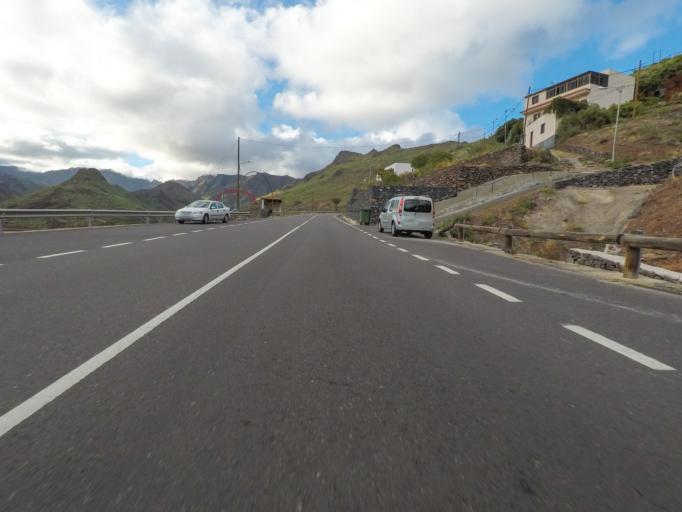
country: ES
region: Canary Islands
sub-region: Provincia de Santa Cruz de Tenerife
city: San Sebastian de la Gomera
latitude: 28.1054
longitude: -17.1243
